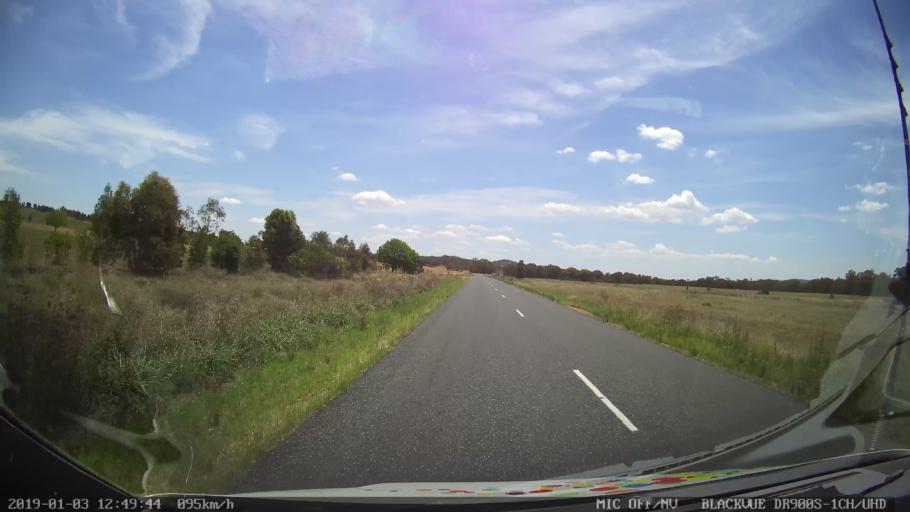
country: AU
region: New South Wales
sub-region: Weddin
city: Grenfell
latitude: -33.6997
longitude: 148.2635
